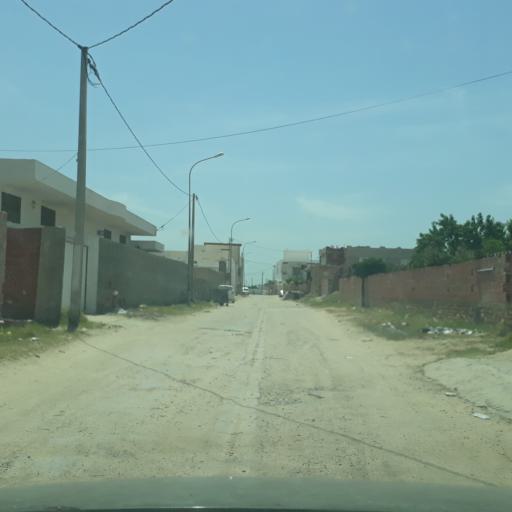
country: TN
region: Safaqis
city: Al Qarmadah
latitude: 34.8249
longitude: 10.7797
